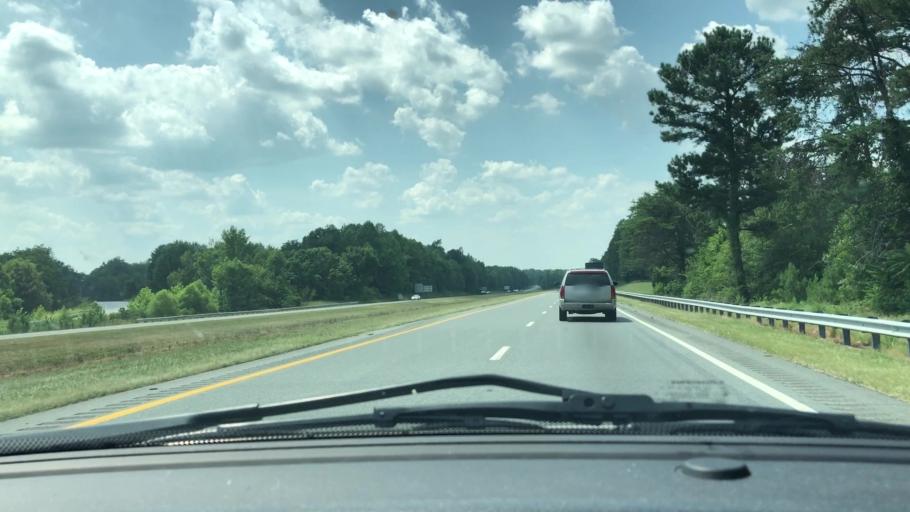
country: US
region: North Carolina
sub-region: Guilford County
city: Forest Oaks
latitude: 35.9703
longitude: -79.7169
